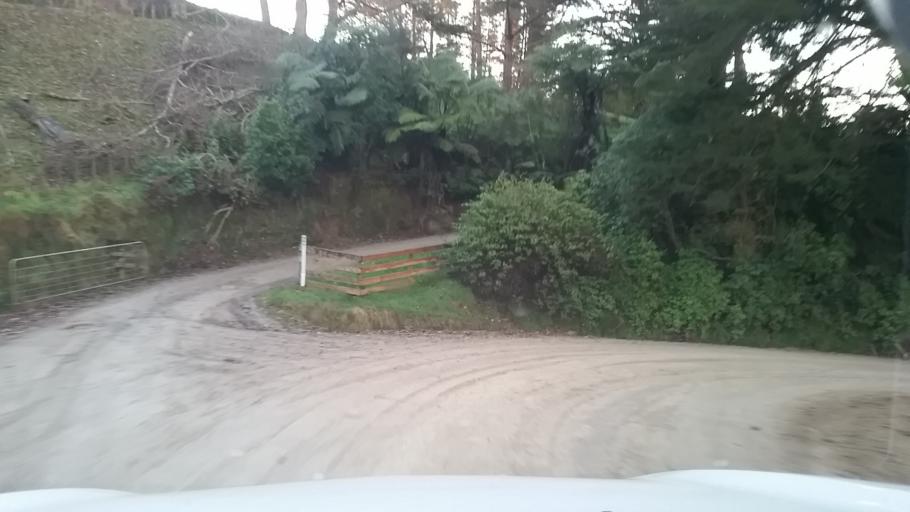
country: NZ
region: Manawatu-Wanganui
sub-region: Wanganui District
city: Wanganui
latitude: -39.7683
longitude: 174.8714
